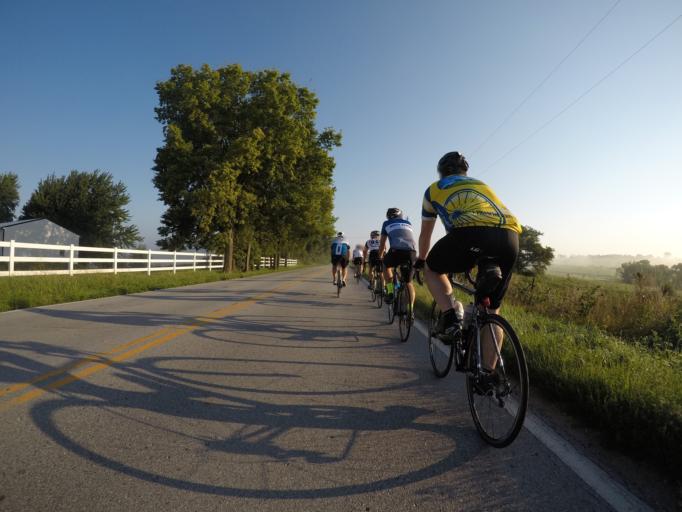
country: US
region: Kansas
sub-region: Leavenworth County
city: Lansing
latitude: 39.2283
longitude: -94.8630
